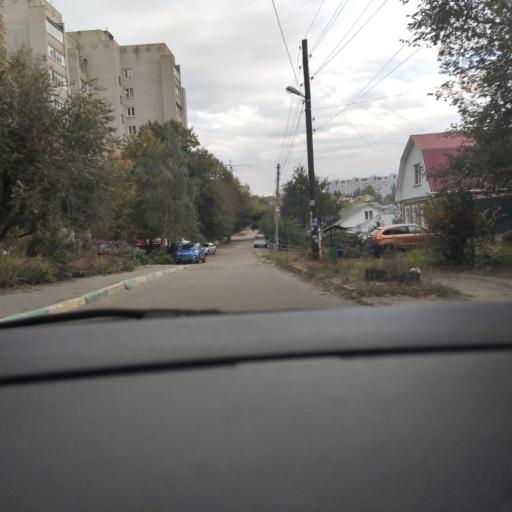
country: RU
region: Voronezj
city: Voronezh
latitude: 51.6896
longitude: 39.1991
